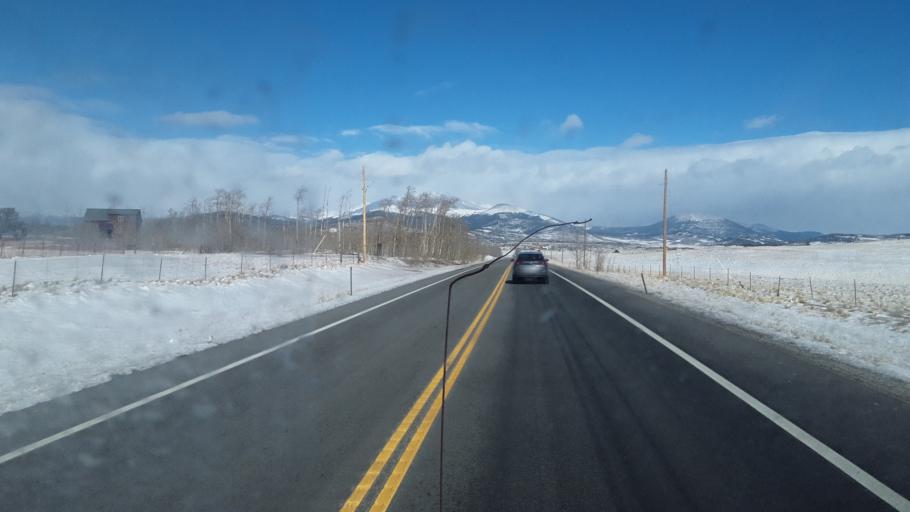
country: US
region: Colorado
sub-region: Park County
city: Fairplay
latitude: 39.1984
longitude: -105.9956
